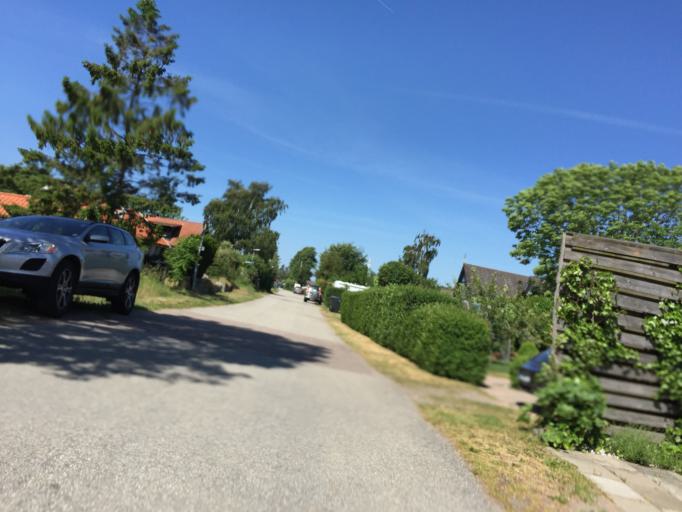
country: SE
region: Skane
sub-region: Trelleborgs Kommun
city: Trelleborg
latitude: 55.3525
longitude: 13.2539
